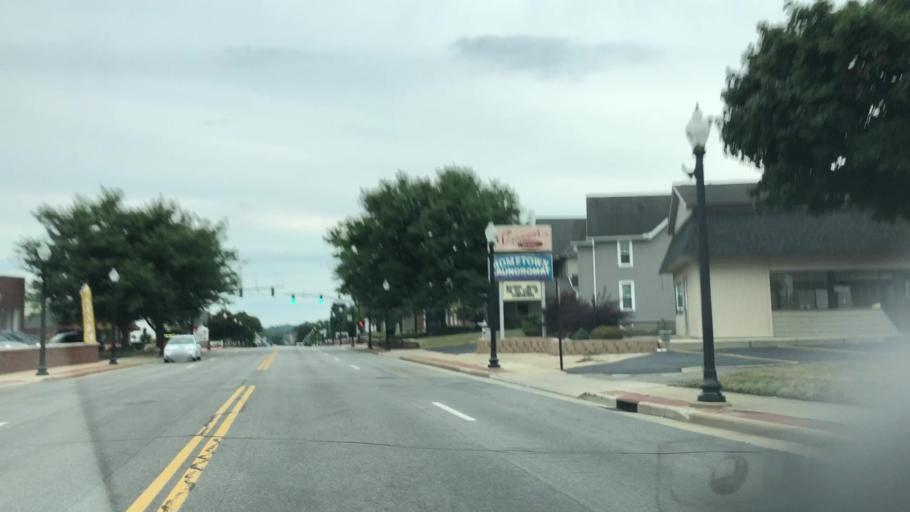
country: US
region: Ohio
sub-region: Stark County
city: North Canton
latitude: 40.8723
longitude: -81.4007
